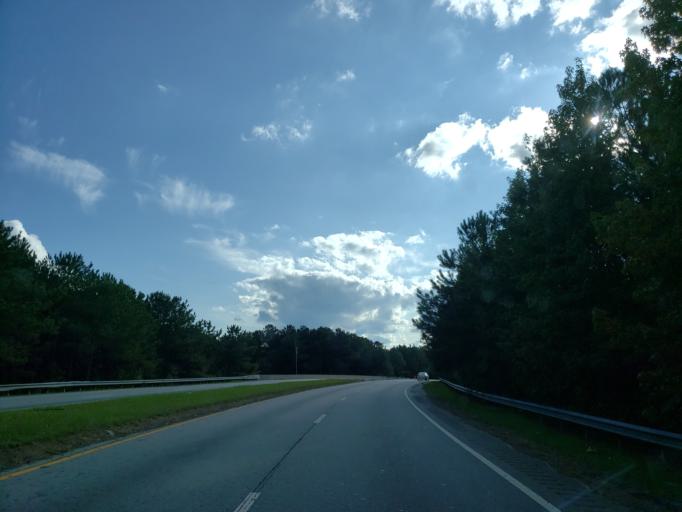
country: US
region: Georgia
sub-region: Cobb County
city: Austell
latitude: 33.8210
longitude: -84.6528
